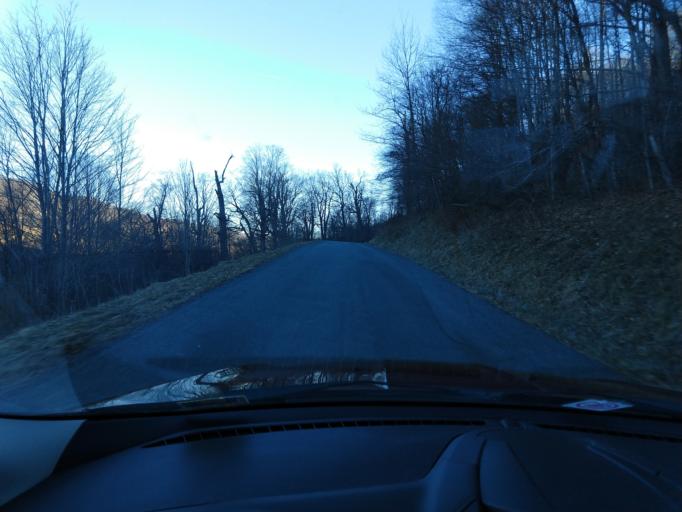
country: US
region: Virginia
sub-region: Highland County
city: Monterey
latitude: 38.4195
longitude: -79.6383
